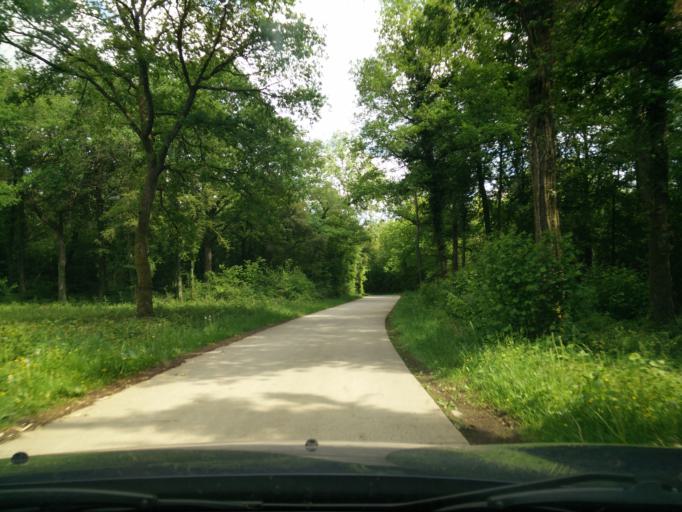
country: FR
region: Champagne-Ardenne
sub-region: Departement des Ardennes
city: Vireux-Molhain
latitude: 50.0876
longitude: 4.6126
